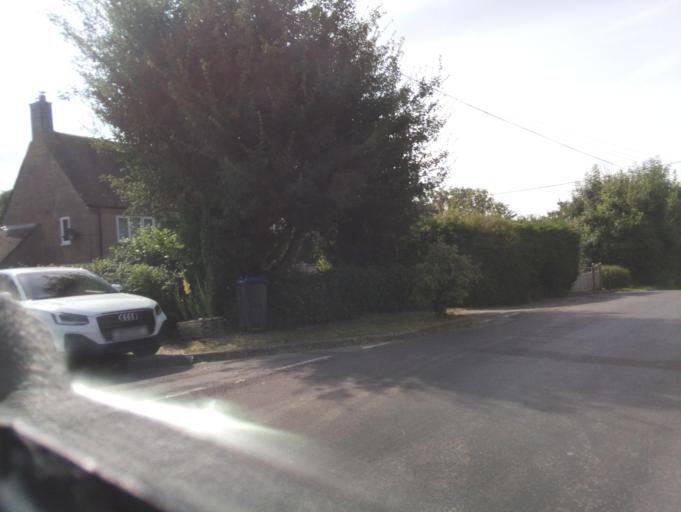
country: GB
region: England
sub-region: Wiltshire
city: Minety
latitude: 51.6171
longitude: -1.9665
